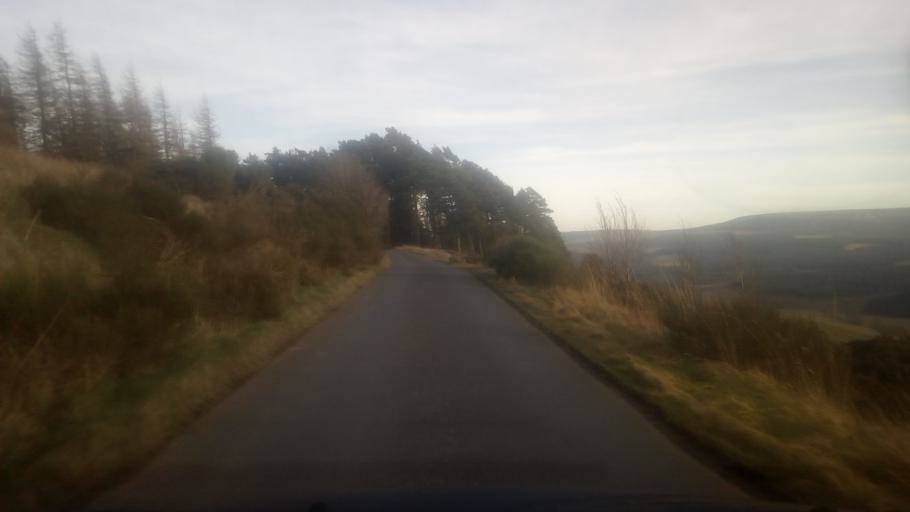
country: GB
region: Scotland
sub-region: The Scottish Borders
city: Jedburgh
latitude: 55.3937
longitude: -2.5693
